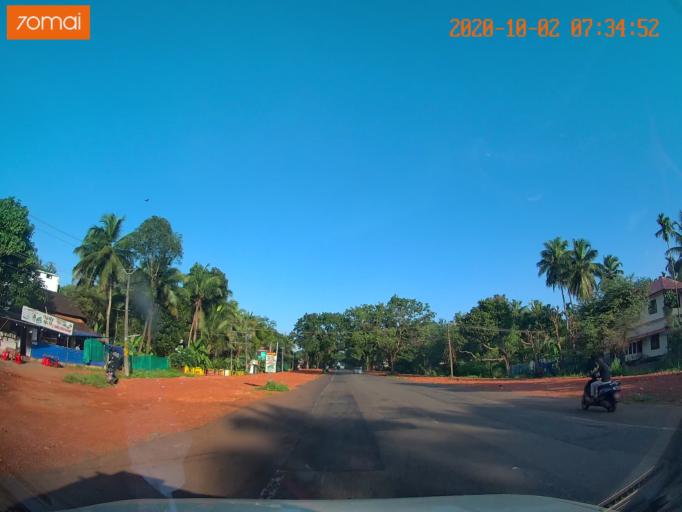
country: IN
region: Kerala
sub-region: Malappuram
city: Pariyapuram
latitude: 11.0659
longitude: 75.9253
